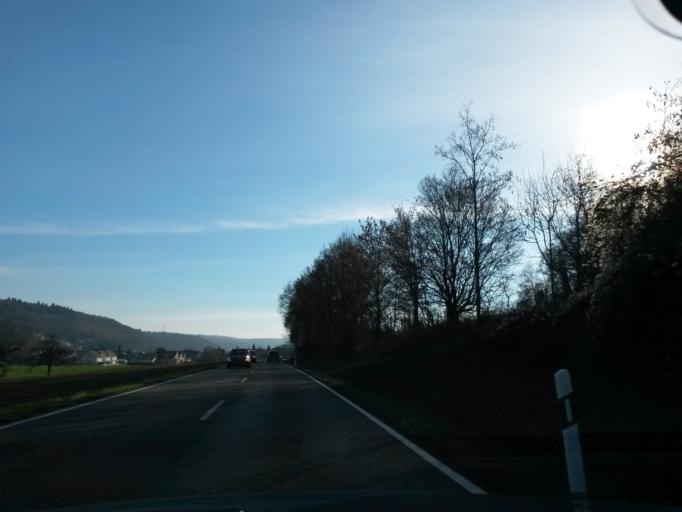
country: DE
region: Baden-Wuerttemberg
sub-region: Karlsruhe Region
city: Konigsbach-Stein
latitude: 48.9558
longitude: 8.6174
